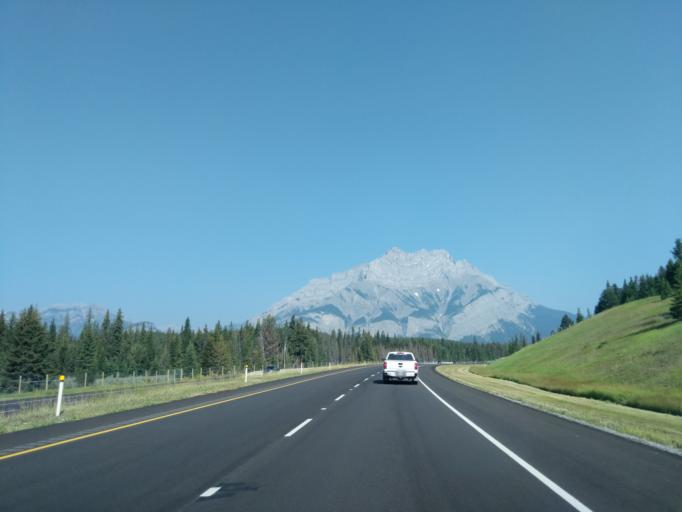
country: CA
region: Alberta
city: Banff
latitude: 51.1812
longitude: -115.4820
